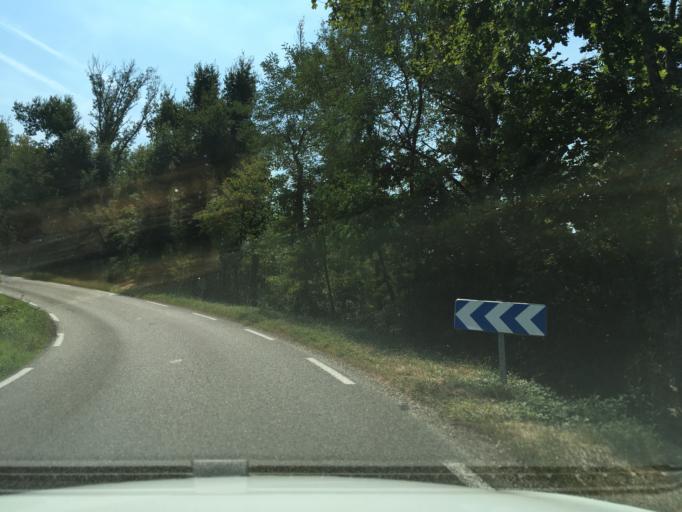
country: FR
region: Midi-Pyrenees
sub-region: Departement du Tarn-et-Garonne
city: Montauban
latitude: 43.9887
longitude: 1.3744
